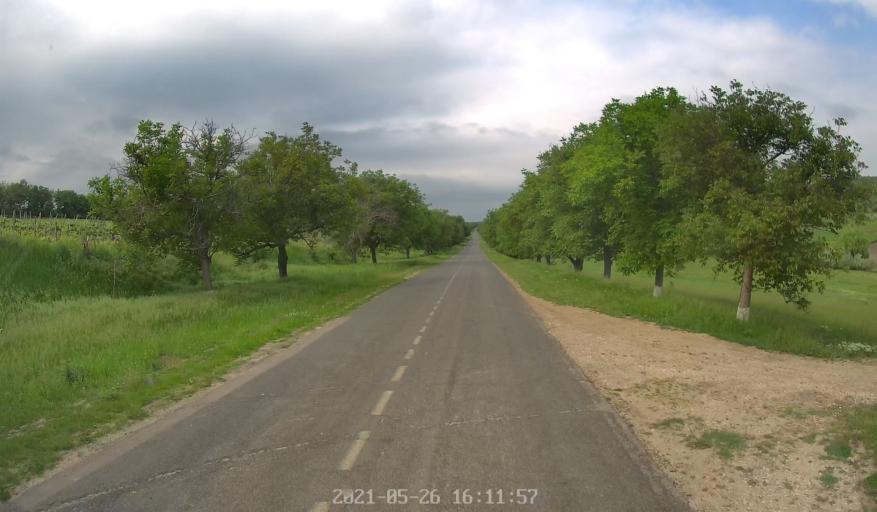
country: MD
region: Hincesti
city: Dancu
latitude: 46.6857
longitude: 28.3357
